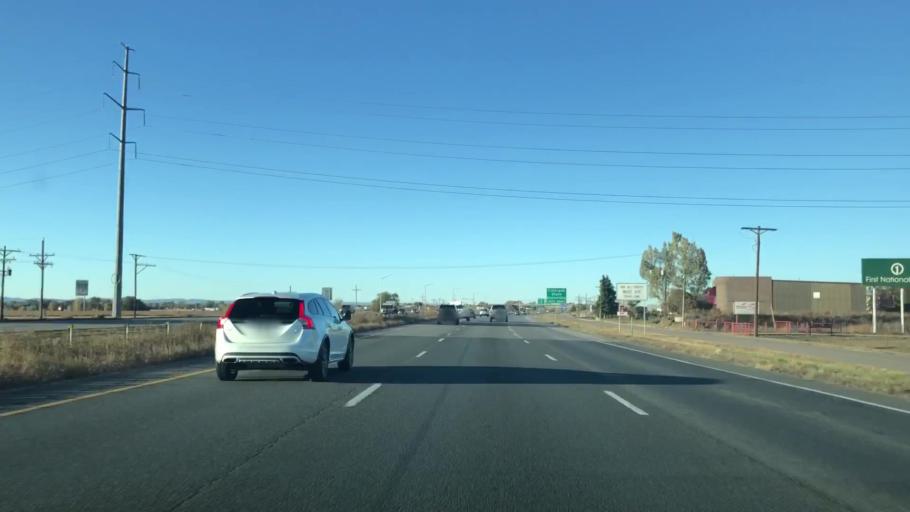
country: US
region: Colorado
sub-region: Larimer County
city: Fort Collins
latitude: 40.5585
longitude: -105.0010
